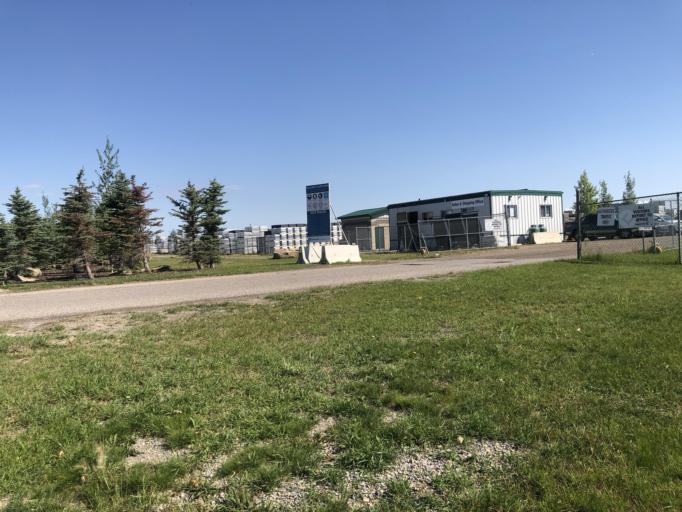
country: CA
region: Alberta
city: Airdrie
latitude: 51.1840
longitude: -113.9348
